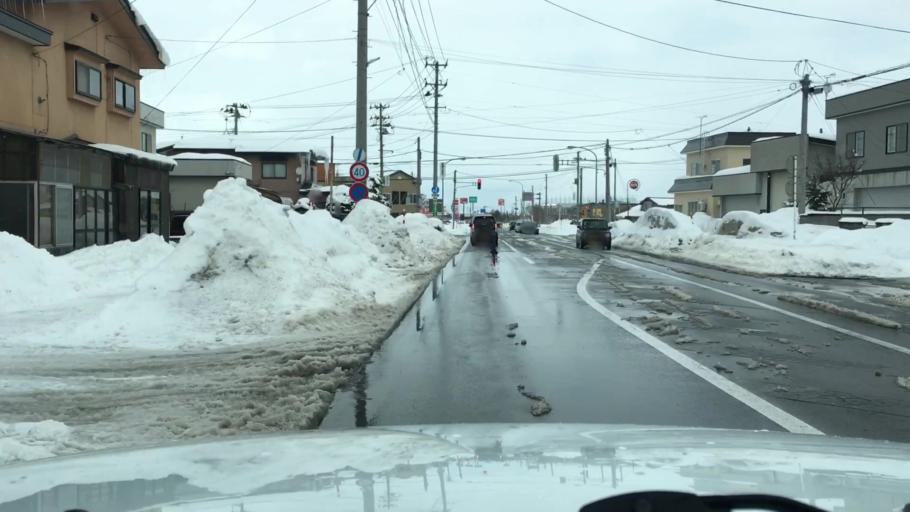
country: JP
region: Aomori
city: Hirosaki
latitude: 40.5814
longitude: 140.4967
